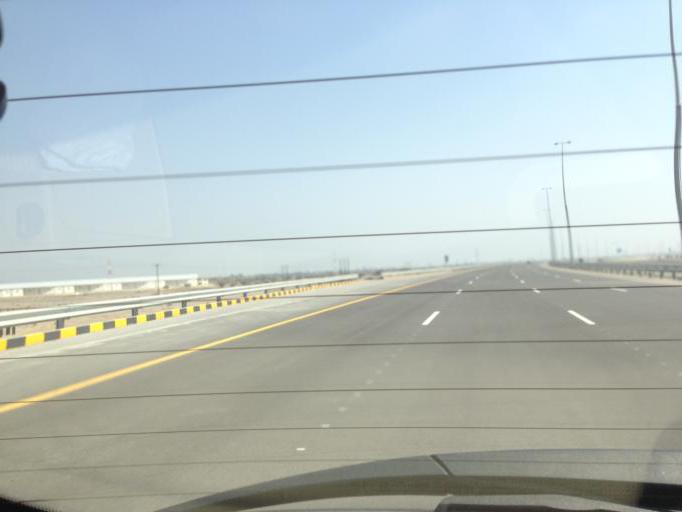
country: OM
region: Al Batinah
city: Barka'
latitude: 23.6284
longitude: 57.8502
